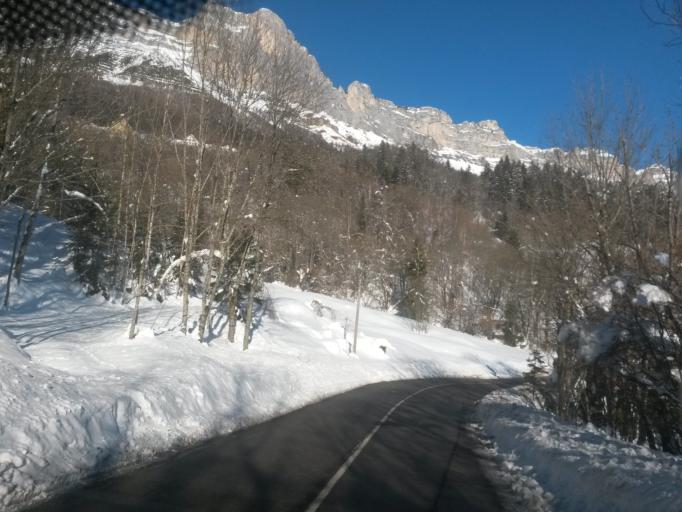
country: FR
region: Rhone-Alpes
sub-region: Departement de l'Isere
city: Saint-Hilaire
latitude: 45.3052
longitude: 5.8800
